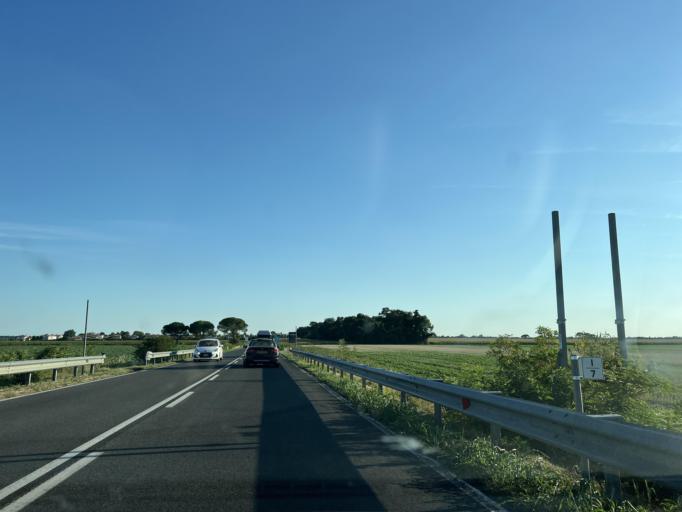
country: IT
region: Friuli Venezia Giulia
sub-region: Provincia di Gorizia
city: San Canzian d'Isonzo
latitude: 45.7647
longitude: 13.4715
